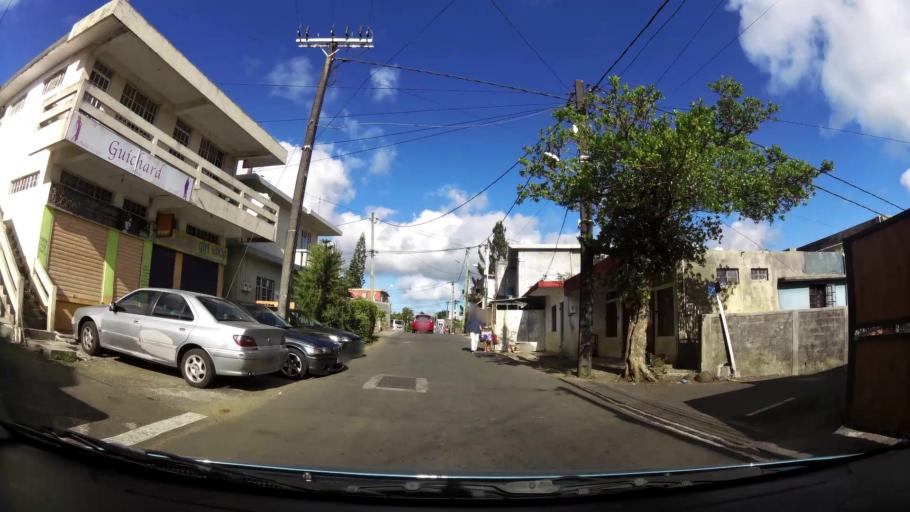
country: MU
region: Plaines Wilhems
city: Curepipe
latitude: -20.3050
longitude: 57.5209
